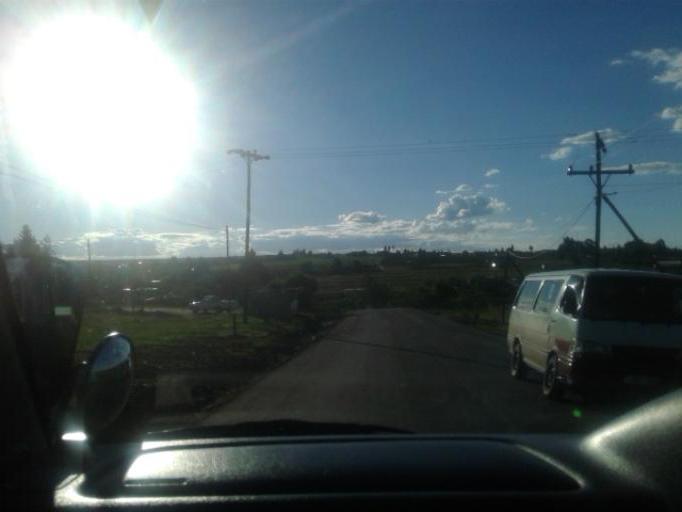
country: LS
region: Maseru
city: Maseru
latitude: -29.3238
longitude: 27.5666
